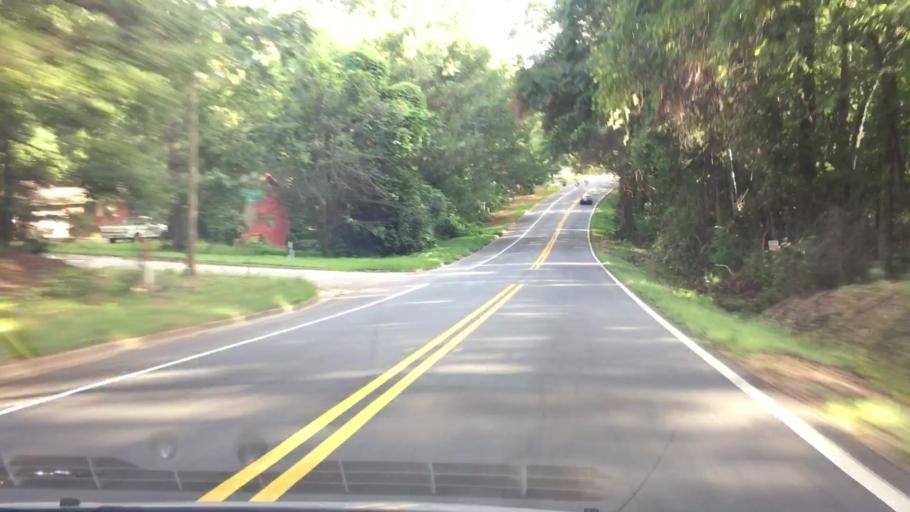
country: US
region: Georgia
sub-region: Clayton County
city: Conley
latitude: 33.6347
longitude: -84.2588
